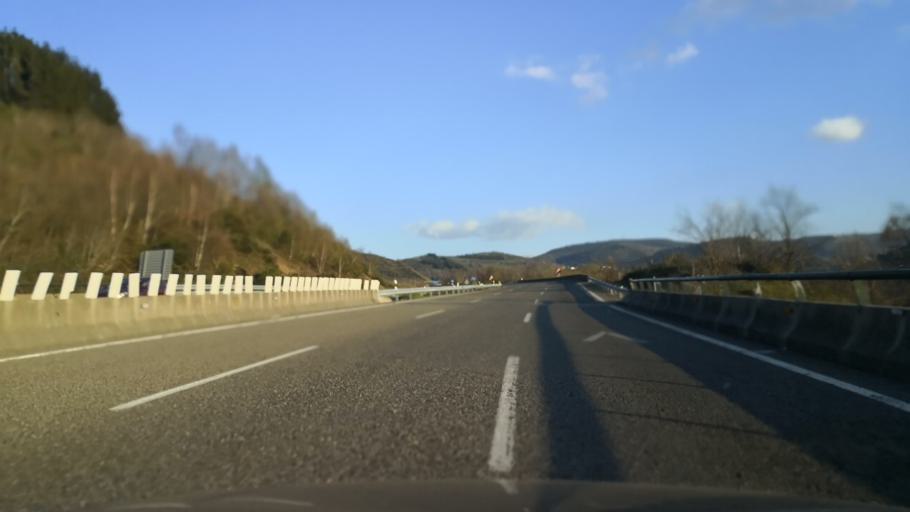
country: ES
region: Galicia
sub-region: Provincia de Lugo
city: San Roman
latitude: 42.7526
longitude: -7.0665
